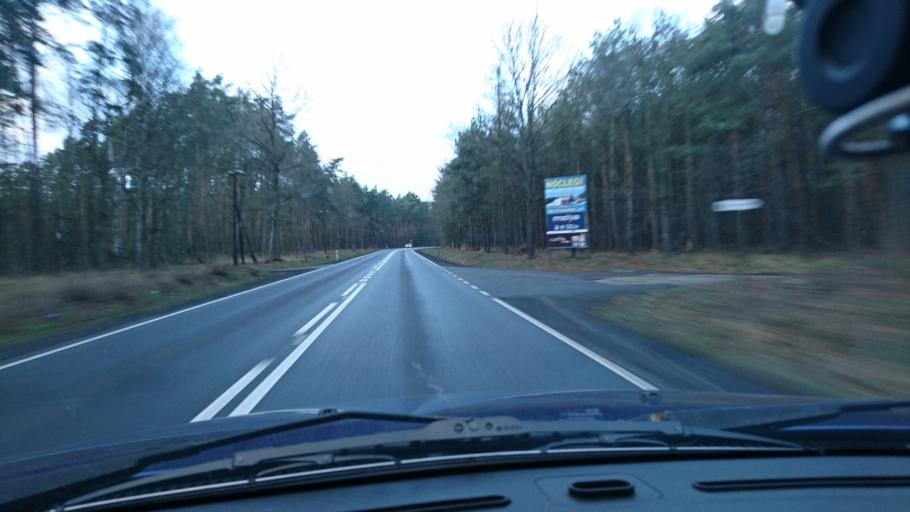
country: PL
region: Greater Poland Voivodeship
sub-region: Powiat kepinski
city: Kepno
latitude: 51.3363
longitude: 17.9546
